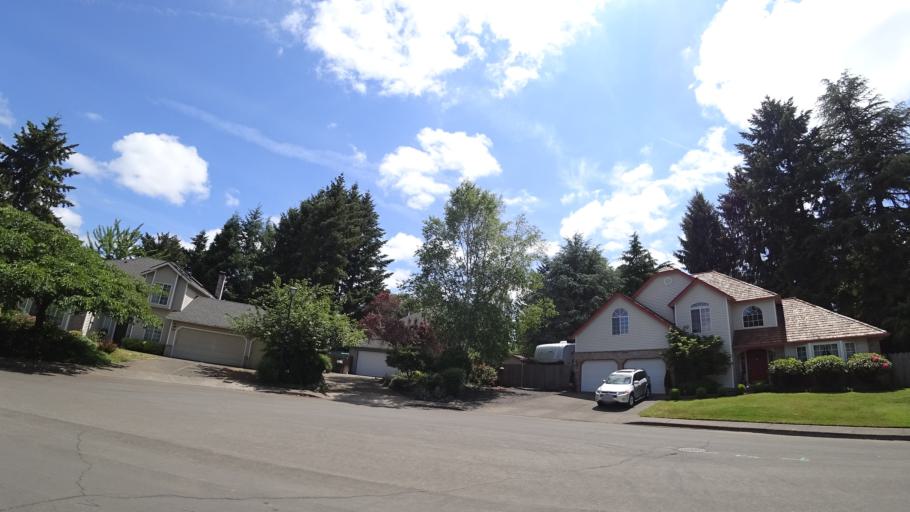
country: US
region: Oregon
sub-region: Washington County
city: King City
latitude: 45.4272
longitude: -122.8011
